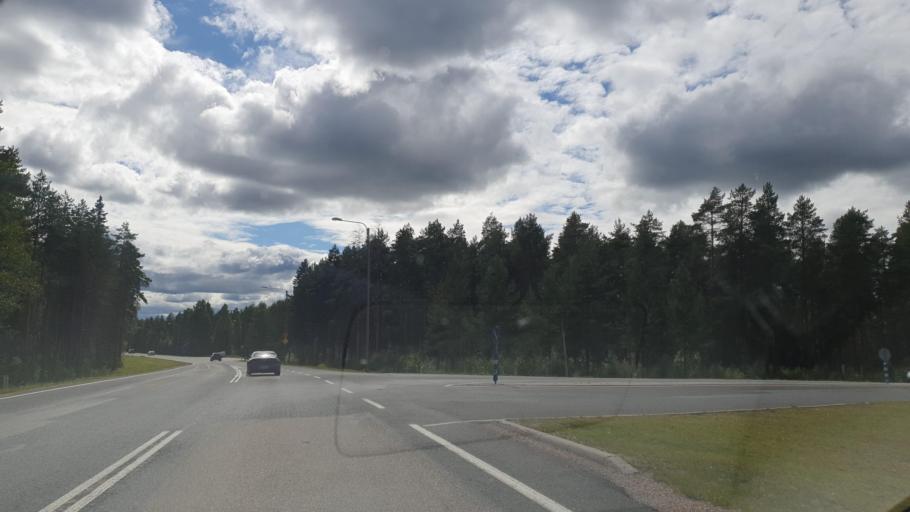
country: FI
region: Kainuu
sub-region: Kajaani
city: Kajaani
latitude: 64.1185
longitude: 27.4511
